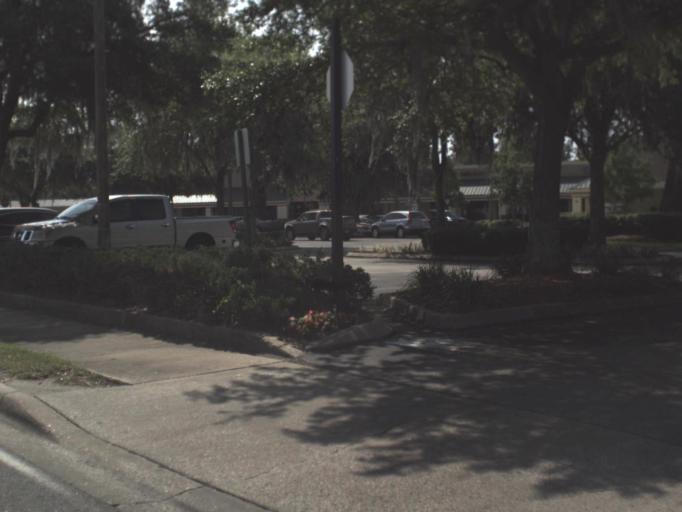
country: US
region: Florida
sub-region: Duval County
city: Jacksonville
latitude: 30.2608
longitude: -81.6443
